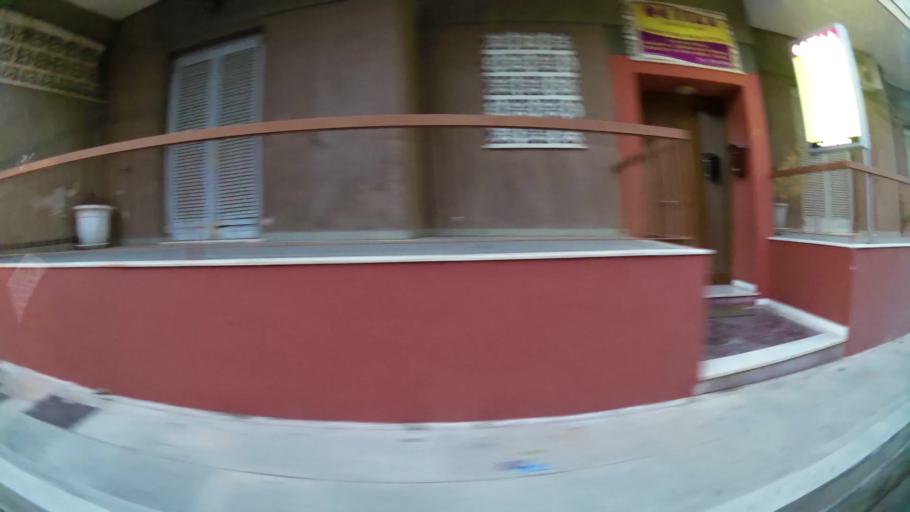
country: GR
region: Attica
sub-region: Nomarchia Anatolikis Attikis
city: Paiania
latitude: 37.9526
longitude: 23.8550
